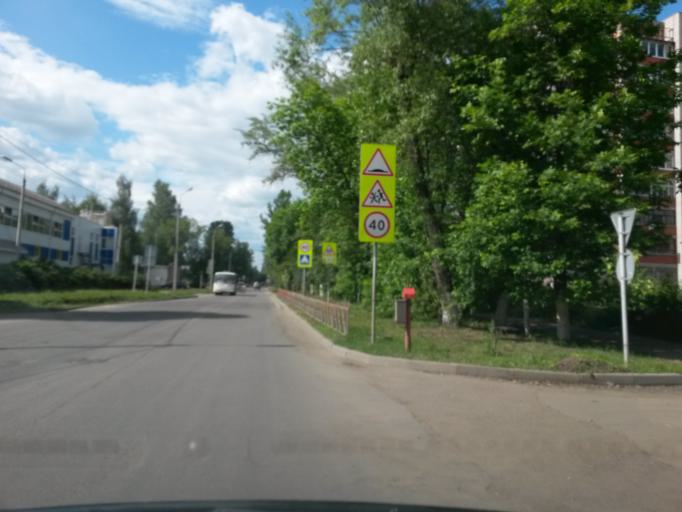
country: RU
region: Jaroslavl
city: Yaroslavl
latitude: 57.6472
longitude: 39.9397
